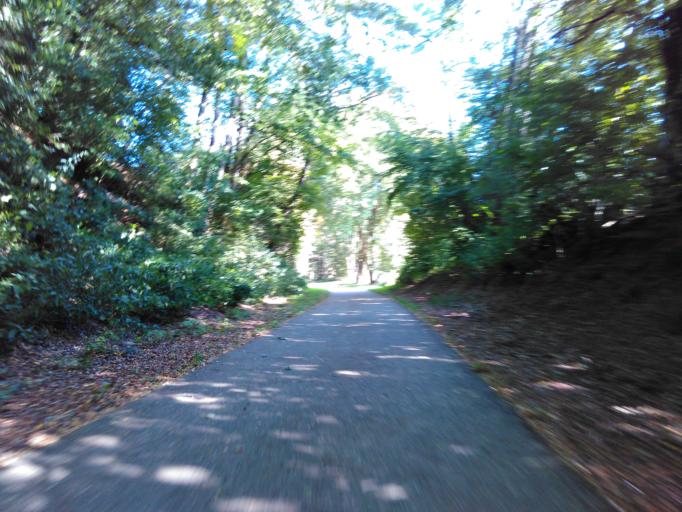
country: LU
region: Luxembourg
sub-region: Canton de Capellen
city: Hobscheid
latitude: 49.6936
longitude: 5.9024
